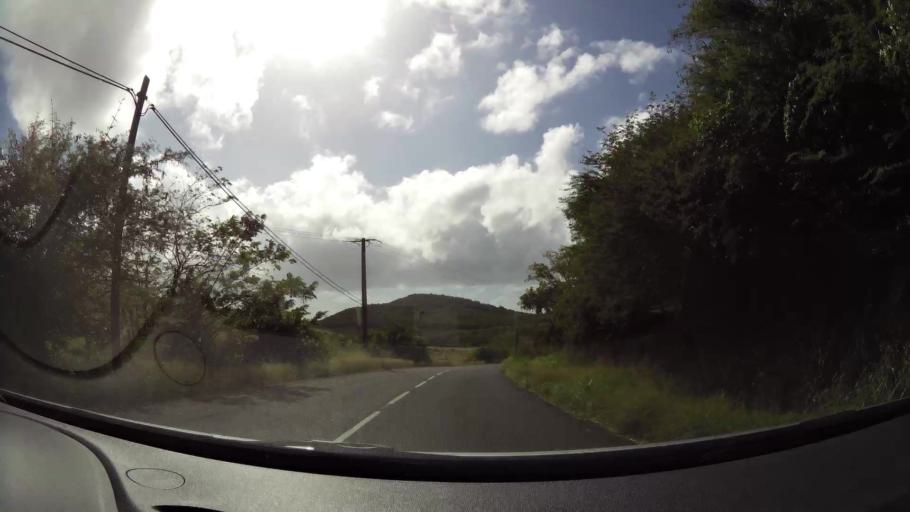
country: MQ
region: Martinique
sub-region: Martinique
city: Le Marin
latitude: 14.4227
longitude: -60.8756
